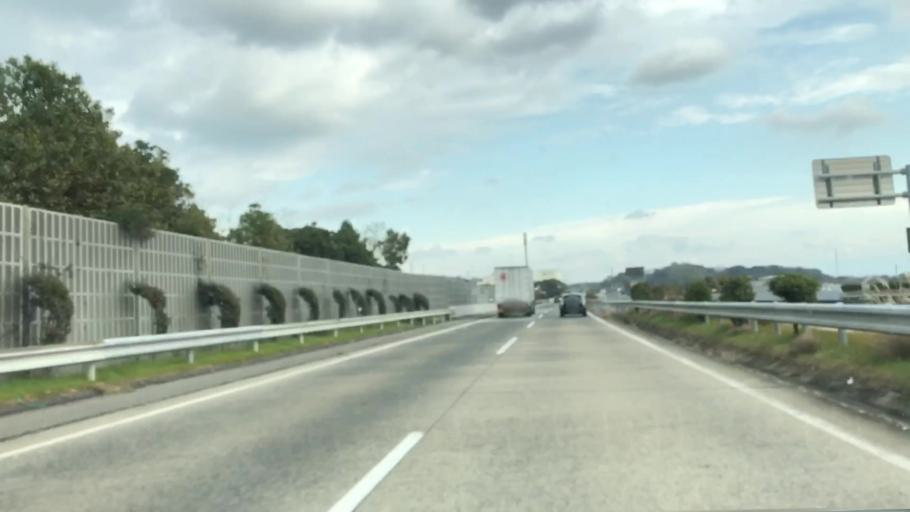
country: JP
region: Saga Prefecture
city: Kanzakimachi-kanzaki
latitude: 33.3543
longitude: 130.3990
